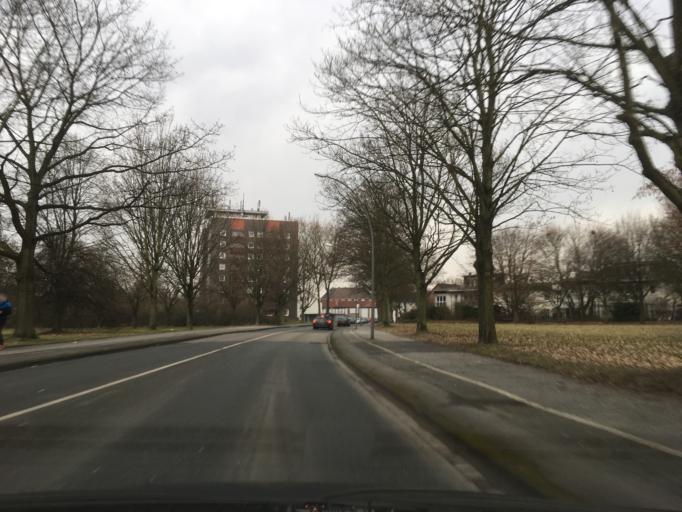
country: DE
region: North Rhine-Westphalia
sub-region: Regierungsbezirk Munster
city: Gladbeck
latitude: 51.5499
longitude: 7.0124
